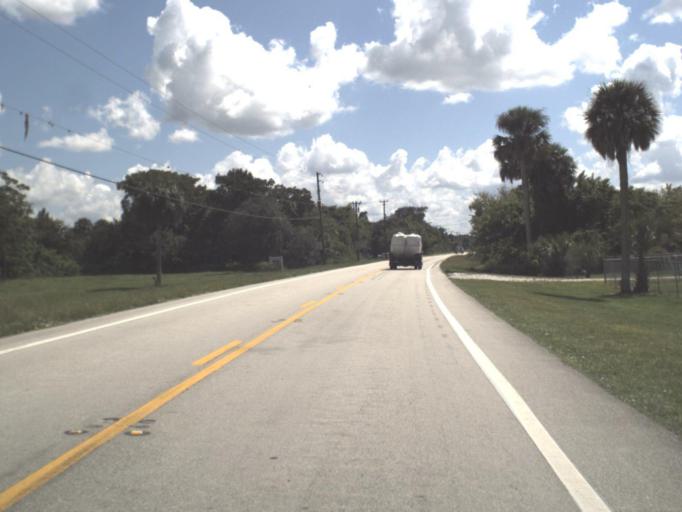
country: US
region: Florida
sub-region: Okeechobee County
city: Taylor Creek
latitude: 27.1496
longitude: -80.6975
